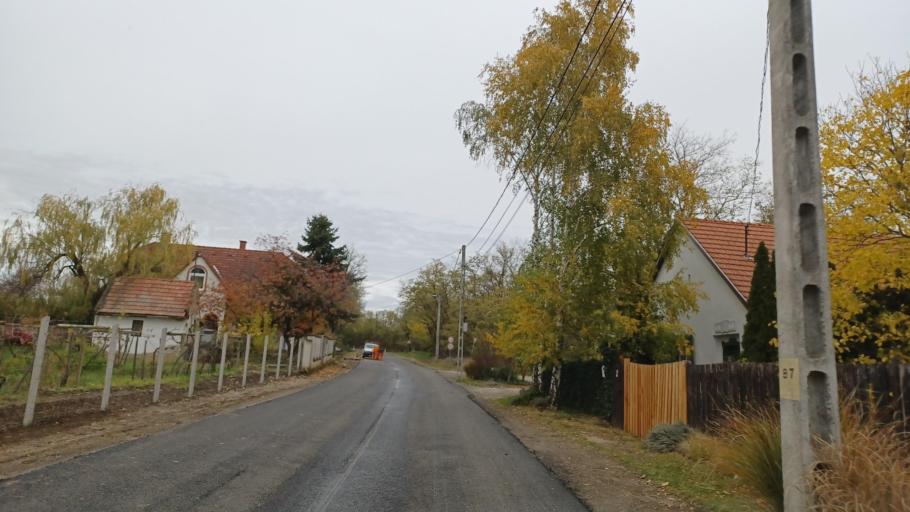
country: HU
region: Tolna
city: Dunaszentgyorgy
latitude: 46.5277
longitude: 18.7683
